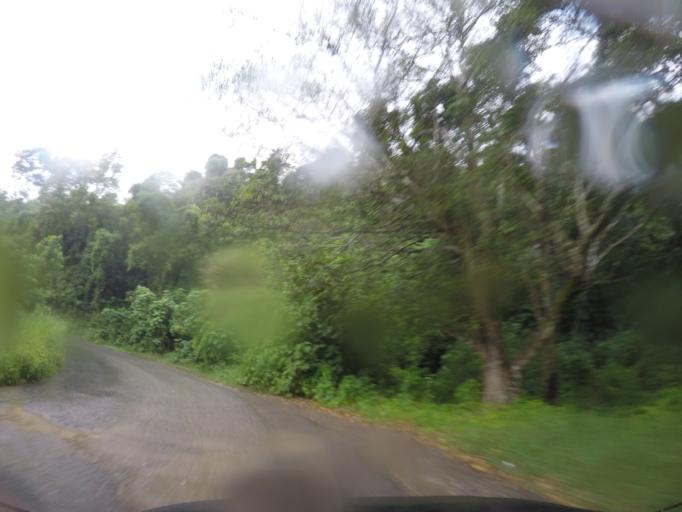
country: MX
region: Oaxaca
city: San Gabriel Mixtepec
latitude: 16.0572
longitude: -97.0809
